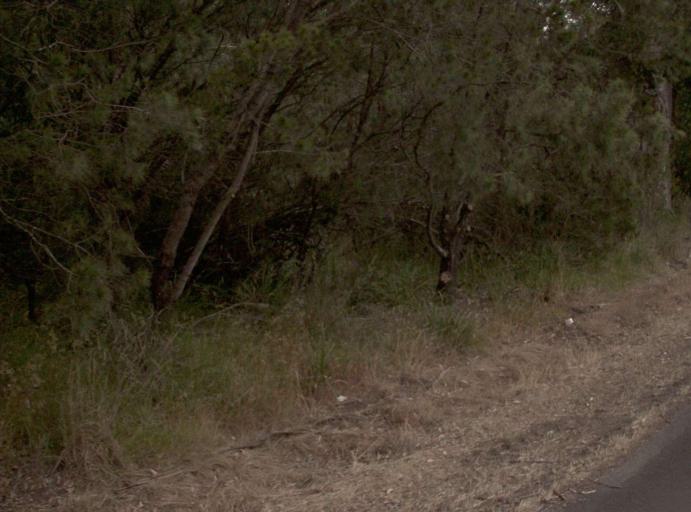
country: AU
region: Victoria
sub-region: Wellington
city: Sale
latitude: -38.4237
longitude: 146.9562
